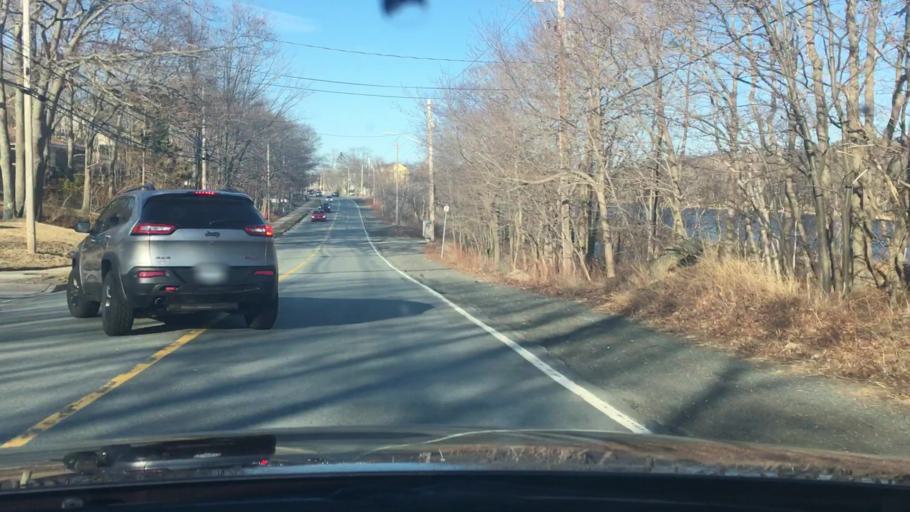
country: CA
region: Nova Scotia
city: Dartmouth
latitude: 44.7424
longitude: -63.6402
